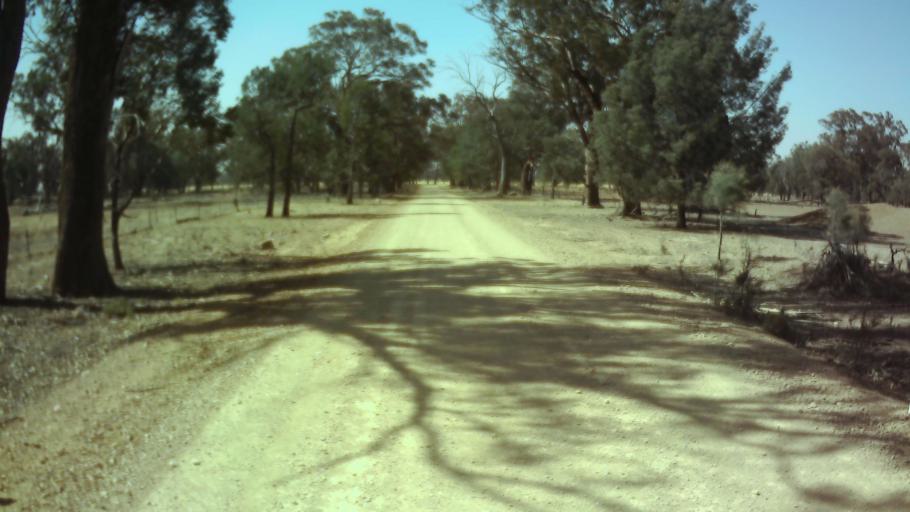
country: AU
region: New South Wales
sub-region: Weddin
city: Grenfell
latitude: -33.9987
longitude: 147.9186
